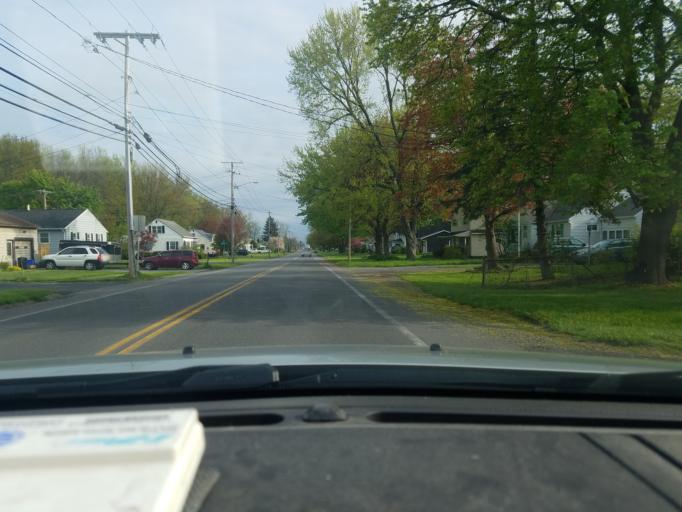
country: US
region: New York
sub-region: Onondaga County
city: East Syracuse
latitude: 43.0771
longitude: -76.0775
